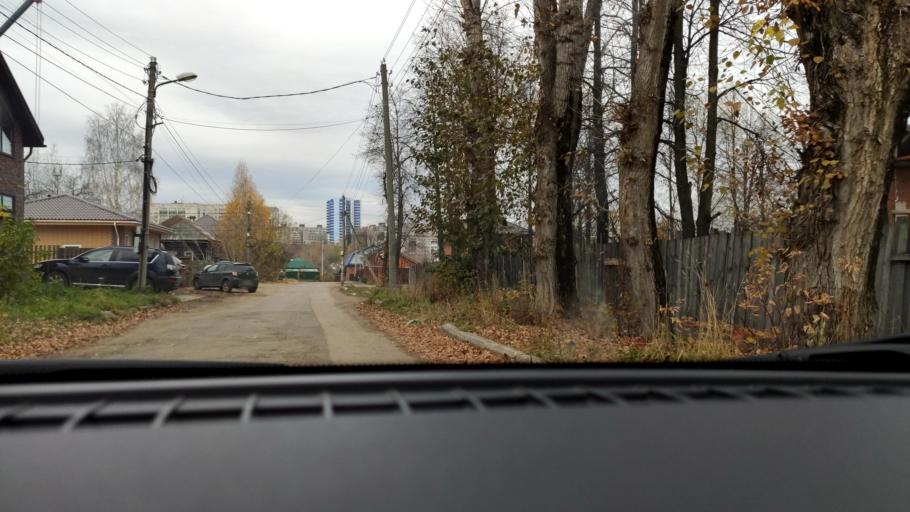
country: RU
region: Perm
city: Perm
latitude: 58.0230
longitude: 56.3158
